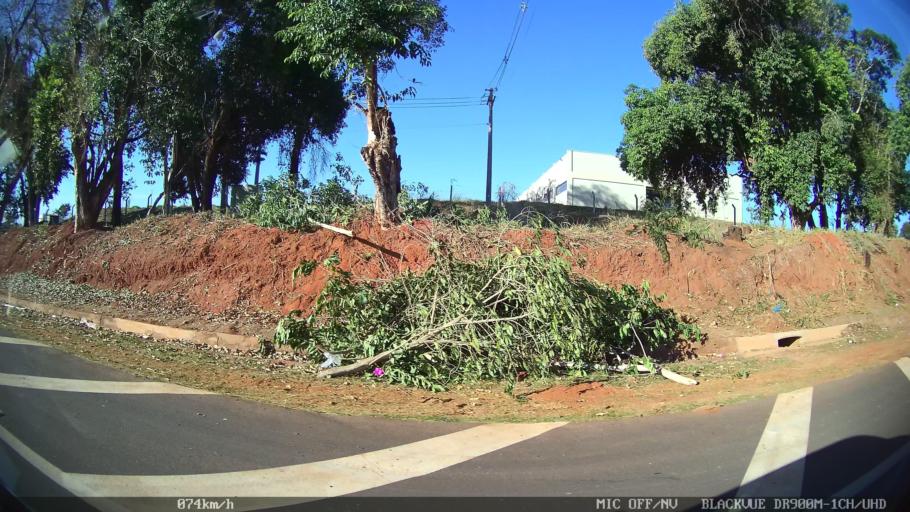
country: BR
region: Sao Paulo
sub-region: Olimpia
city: Olimpia
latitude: -20.7107
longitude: -48.9099
